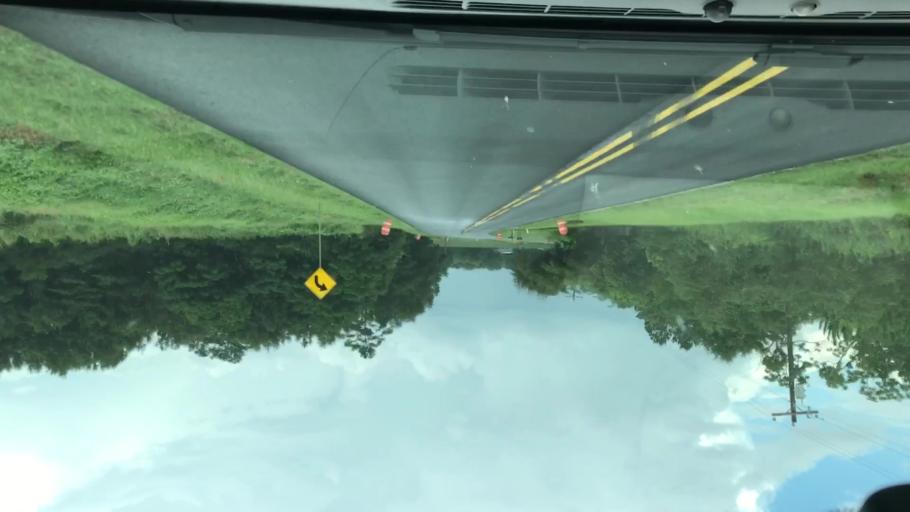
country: US
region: Georgia
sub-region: Early County
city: Blakely
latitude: 31.4180
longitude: -84.9630
